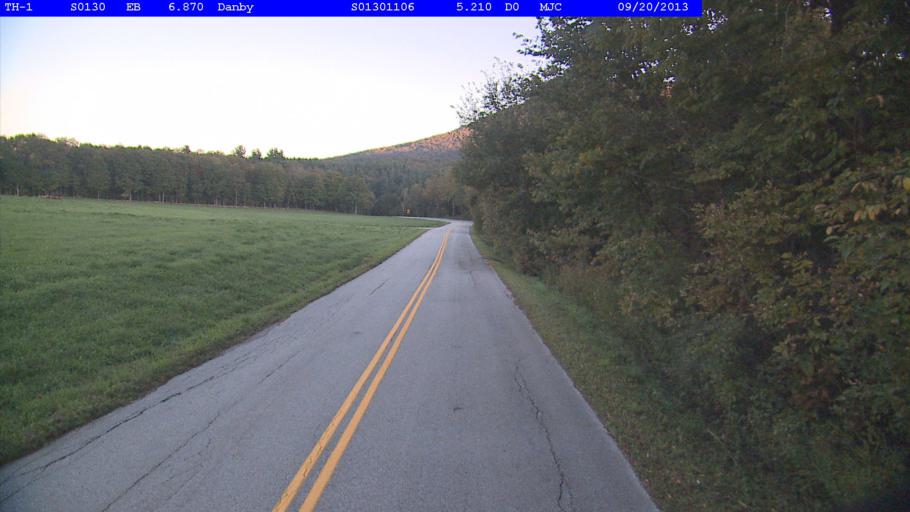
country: US
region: Vermont
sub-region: Bennington County
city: Manchester Center
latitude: 43.3414
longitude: -73.0443
